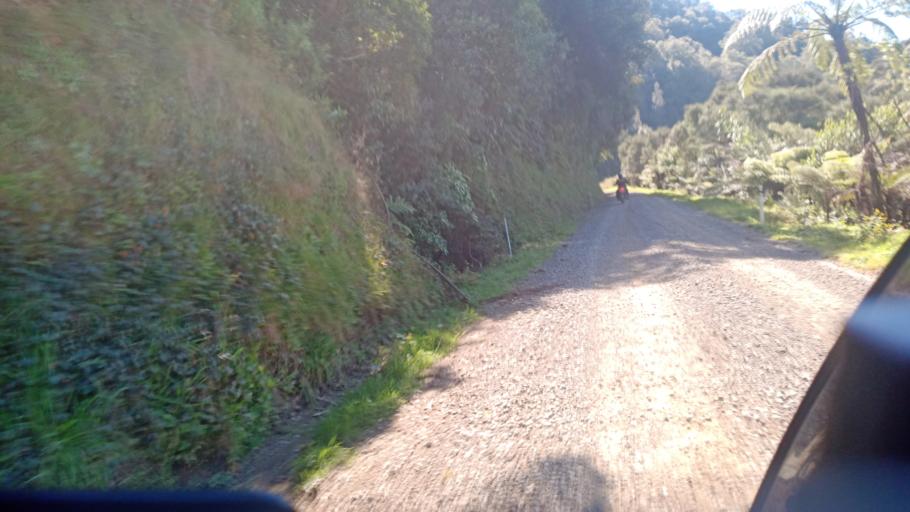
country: NZ
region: Bay of Plenty
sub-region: Opotiki District
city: Opotiki
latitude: -38.0383
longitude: 177.4415
